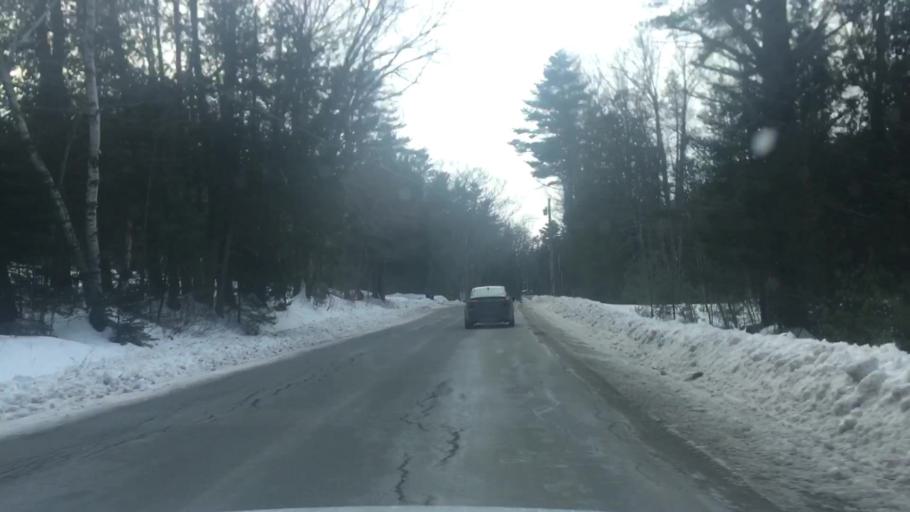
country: US
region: Maine
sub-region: Hancock County
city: Orland
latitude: 44.6184
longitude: -68.7061
